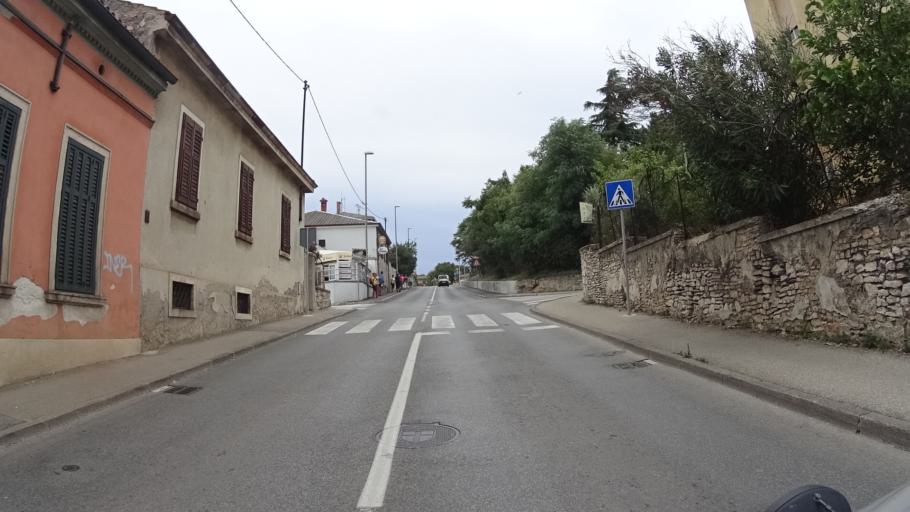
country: HR
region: Istarska
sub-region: Grad Pula
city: Pula
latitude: 44.8594
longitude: 13.8452
